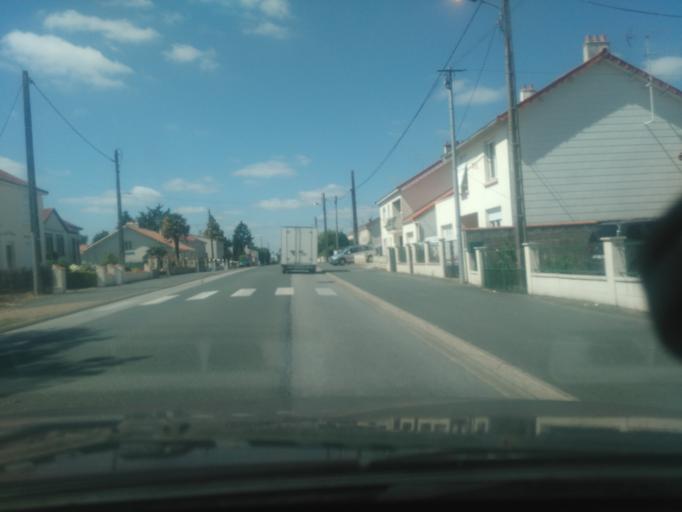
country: FR
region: Pays de la Loire
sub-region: Departement de la Vendee
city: La Ferriere
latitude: 46.7183
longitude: -1.3071
